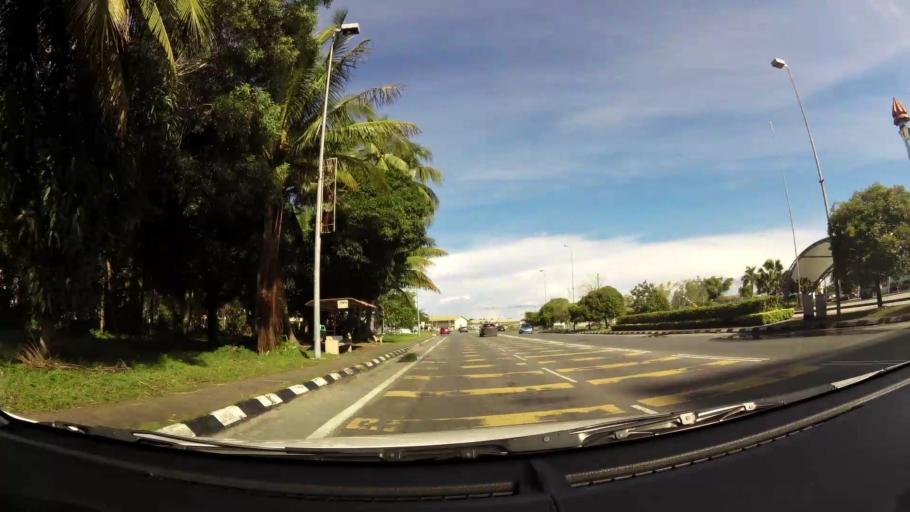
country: BN
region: Belait
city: Kuala Belait
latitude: 4.5781
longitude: 114.1967
